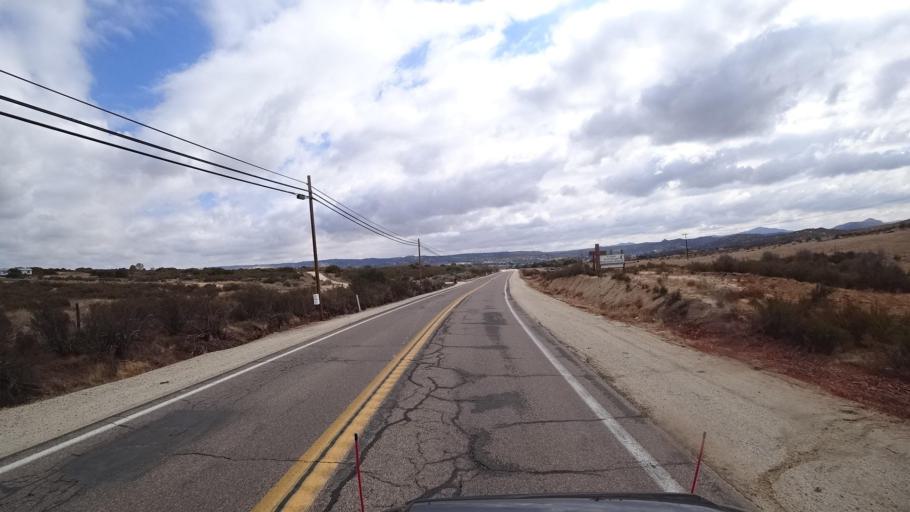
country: US
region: California
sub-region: San Diego County
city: Campo
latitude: 32.6385
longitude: -116.4799
